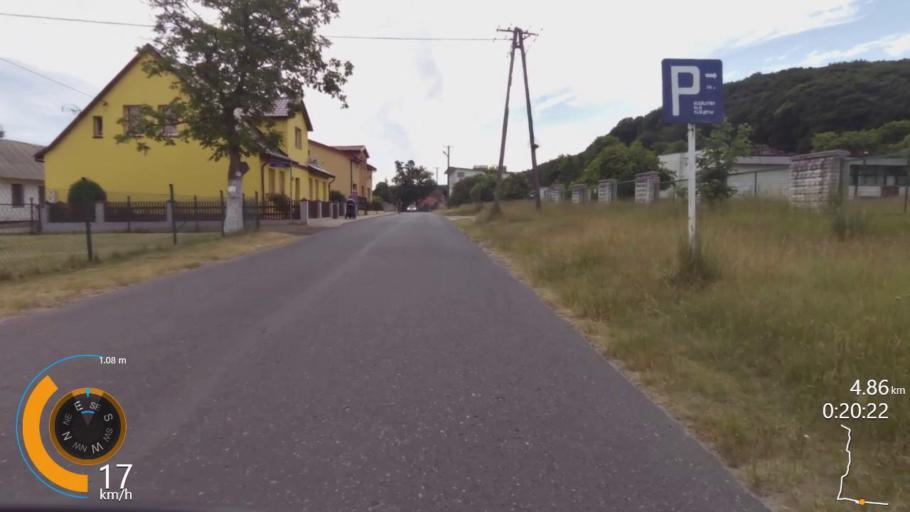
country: PL
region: West Pomeranian Voivodeship
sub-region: Powiat kamienski
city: Miedzyzdroje
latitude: 53.8793
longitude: 14.4424
